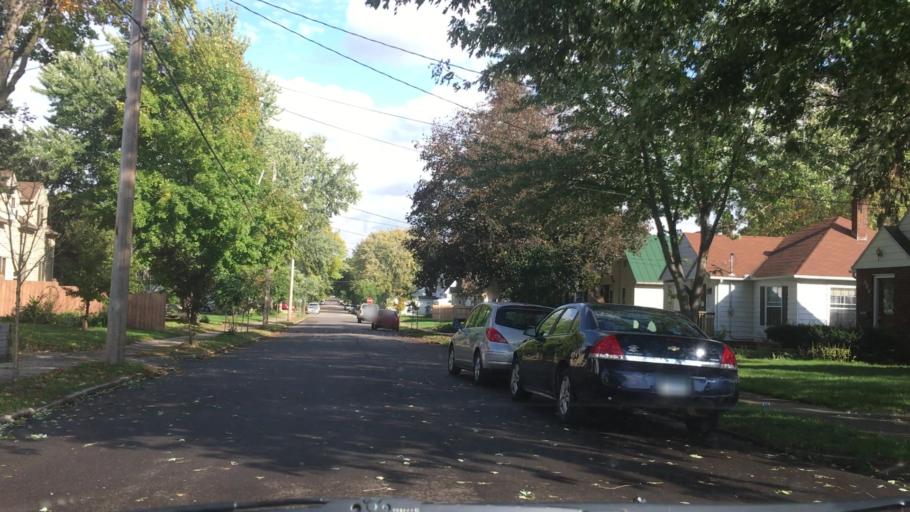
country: US
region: Minnesota
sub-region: Olmsted County
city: Rochester
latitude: 44.0108
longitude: -92.4605
